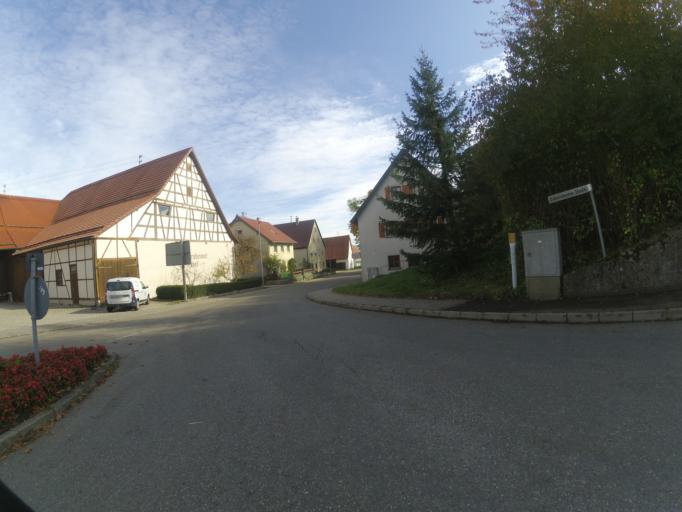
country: DE
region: Baden-Wuerttemberg
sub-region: Tuebingen Region
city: Amstetten
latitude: 48.5947
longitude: 9.9176
